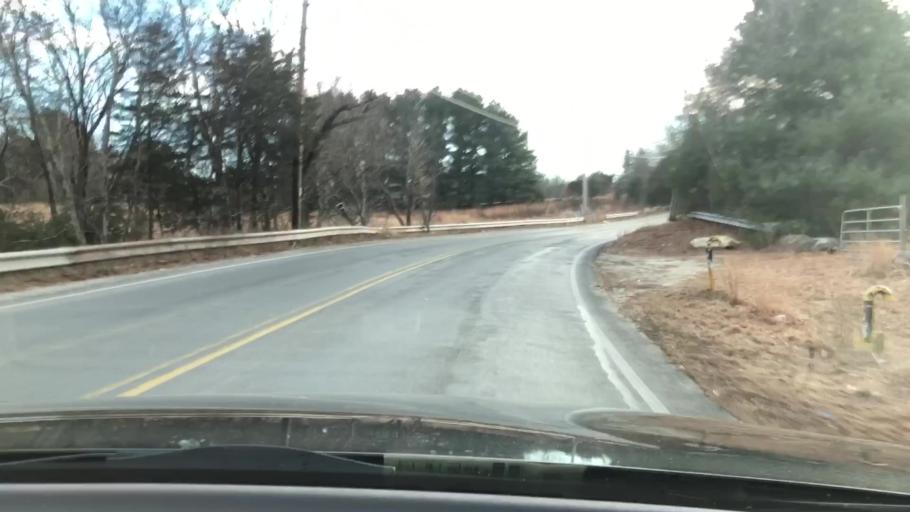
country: US
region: Massachusetts
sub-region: Worcester County
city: Mendon
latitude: 42.0661
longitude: -71.5243
